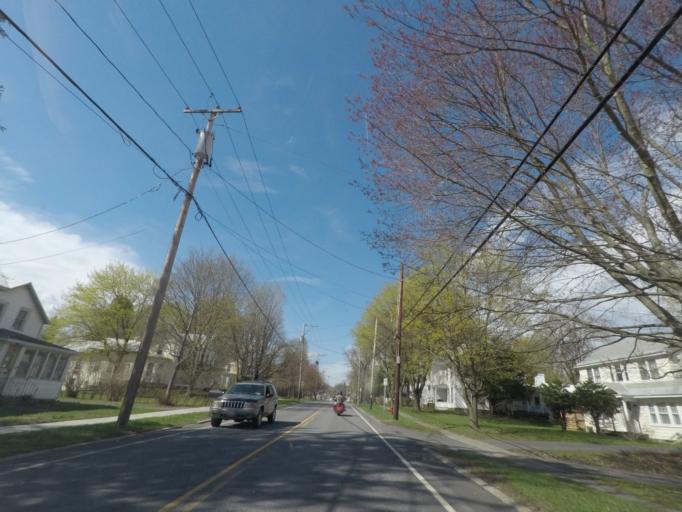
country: US
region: New York
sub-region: Greene County
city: Cairo
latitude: 42.4132
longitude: -74.0219
